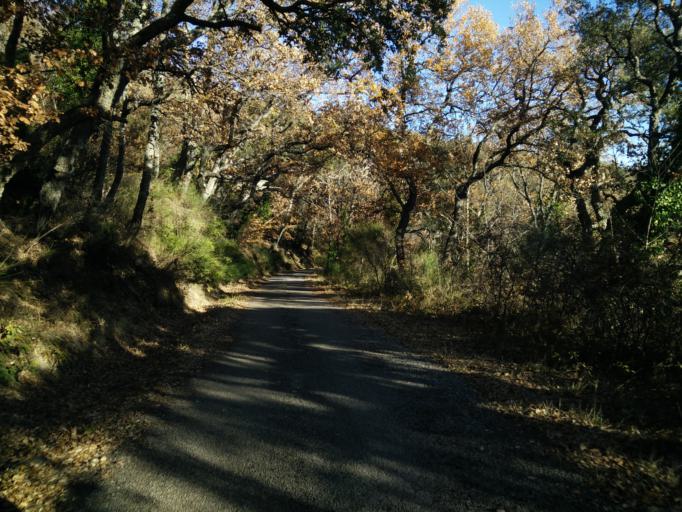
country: FR
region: Provence-Alpes-Cote d'Azur
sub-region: Departement du Var
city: Gonfaron
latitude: 43.2787
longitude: 6.2922
